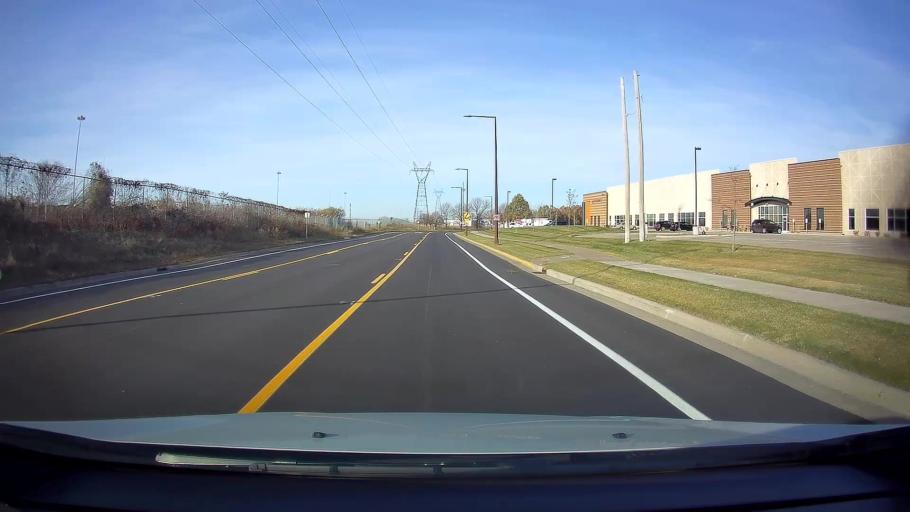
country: US
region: Minnesota
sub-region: Ramsey County
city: Falcon Heights
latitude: 44.9722
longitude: -93.1749
